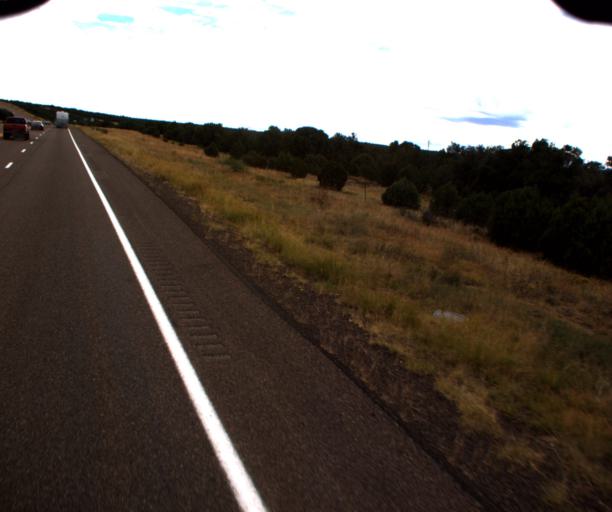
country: US
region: Arizona
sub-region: Navajo County
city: White Mountain Lake
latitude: 34.3538
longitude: -110.0536
